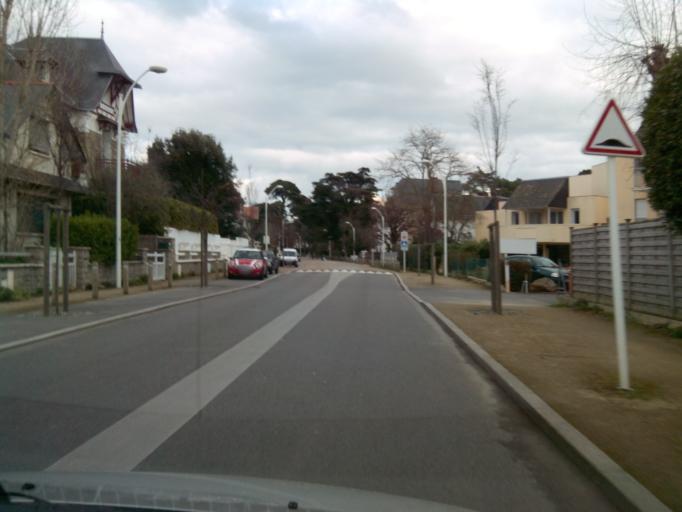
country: FR
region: Pays de la Loire
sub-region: Departement de la Loire-Atlantique
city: Le Pouliguen
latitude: 47.2775
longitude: -2.4236
